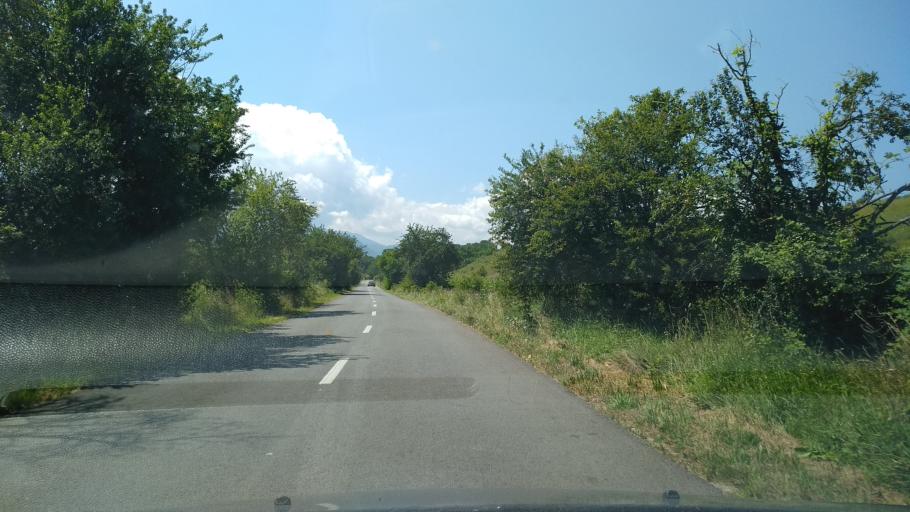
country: RO
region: Hunedoara
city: Salasu de Sus
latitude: 45.5387
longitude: 22.9793
